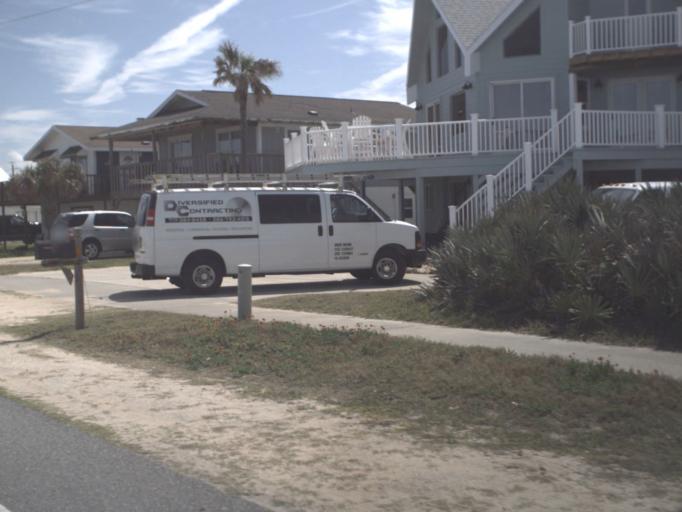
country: US
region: Florida
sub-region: Flagler County
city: Flagler Beach
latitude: 29.4561
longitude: -81.1157
